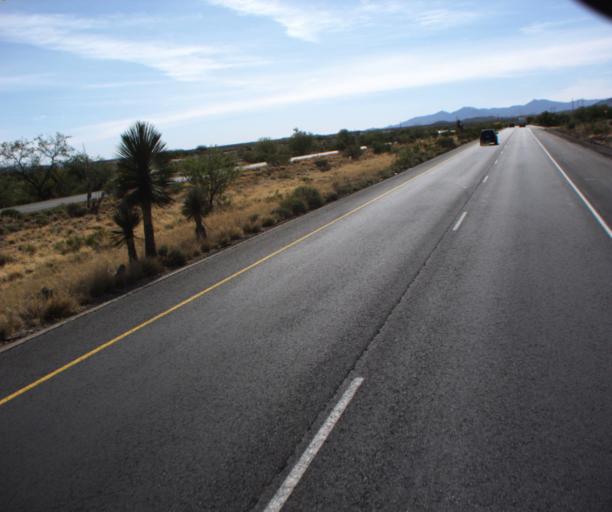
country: US
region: Arizona
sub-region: Pima County
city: Vail
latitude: 32.0065
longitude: -110.6898
